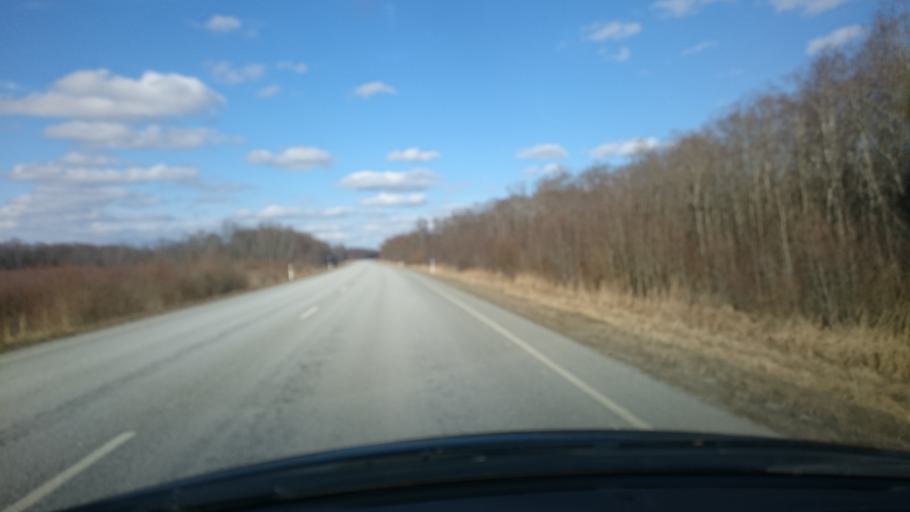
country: EE
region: Laeaene
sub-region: Lihula vald
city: Lihula
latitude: 58.6887
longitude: 23.8140
